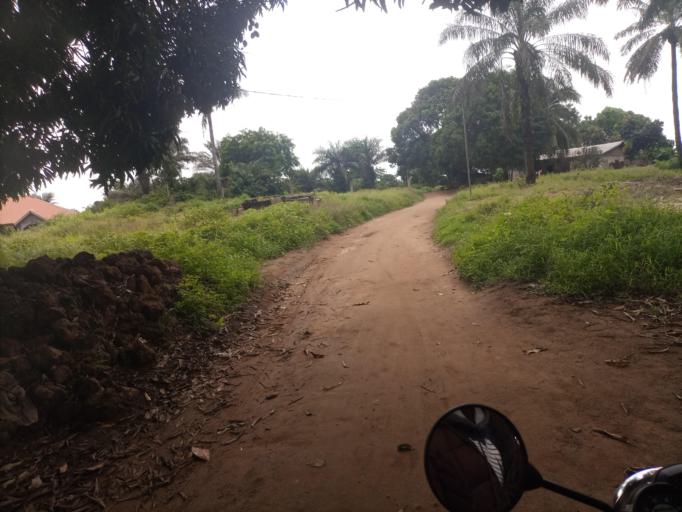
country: SL
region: Northern Province
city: Masoyila
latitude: 8.5697
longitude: -13.1609
